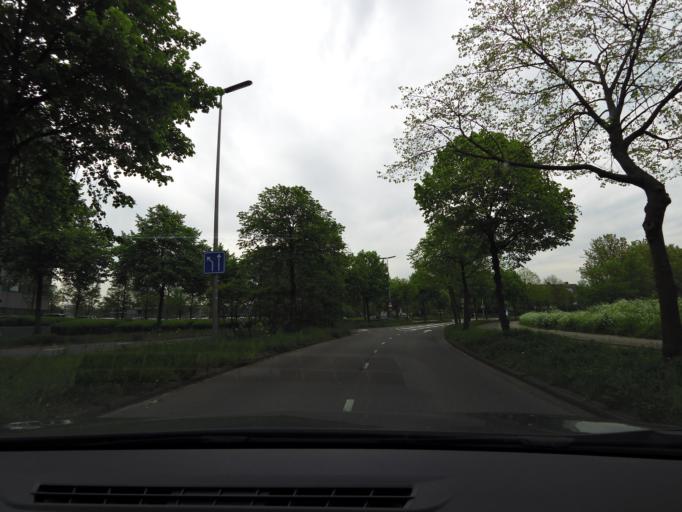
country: NL
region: South Holland
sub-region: Gemeente Delft
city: Delft
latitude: 51.9848
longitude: 4.3452
